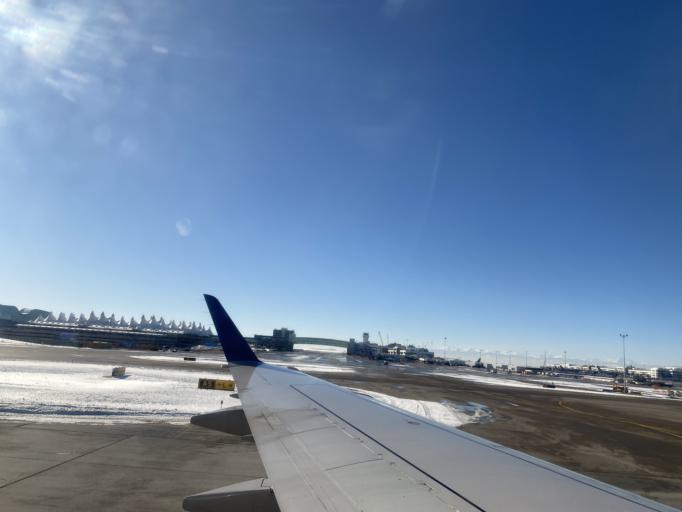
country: US
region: Colorado
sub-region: Weld County
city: Lochbuie
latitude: 39.8525
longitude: -104.6624
